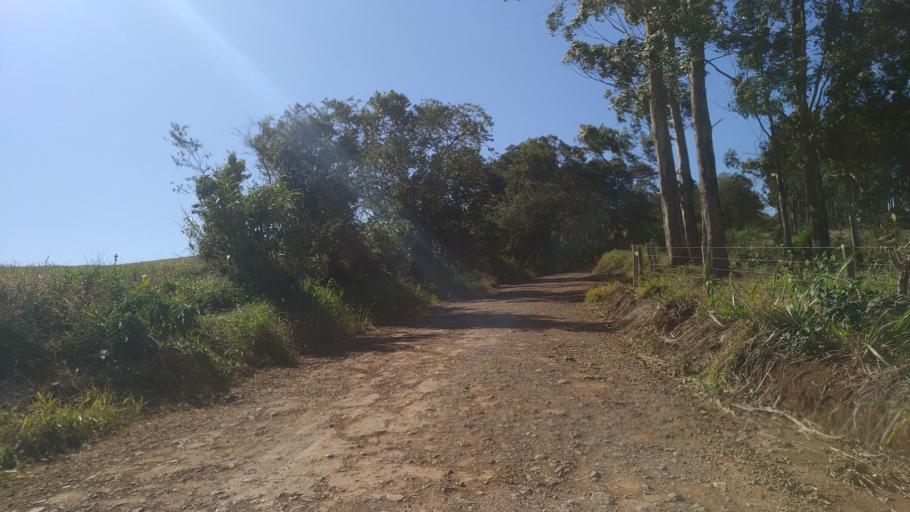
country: BR
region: Santa Catarina
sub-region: Chapeco
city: Chapeco
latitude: -27.1490
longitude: -52.6109
